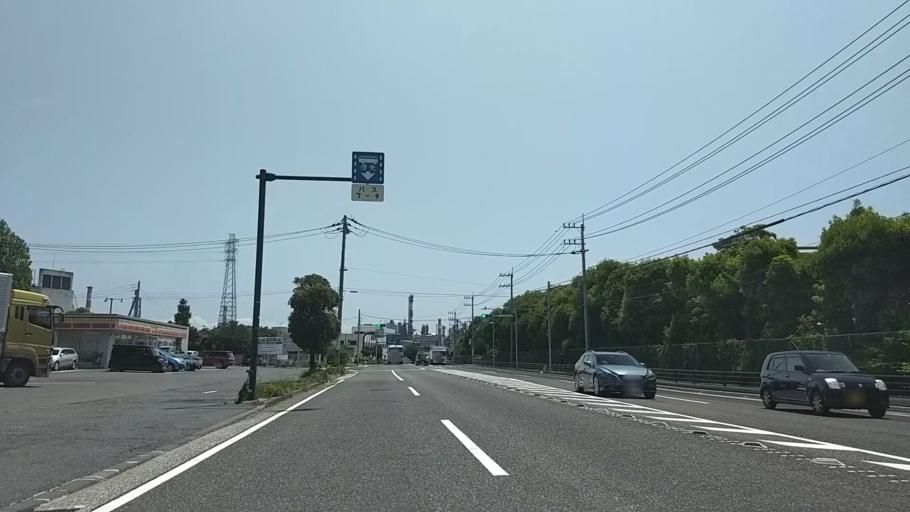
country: JP
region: Kanagawa
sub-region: Kawasaki-shi
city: Kawasaki
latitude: 35.5185
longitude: 139.7348
